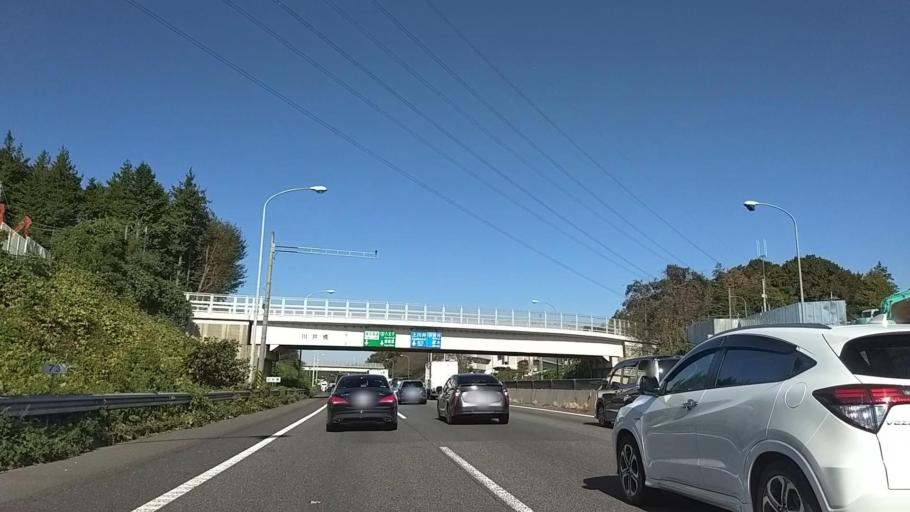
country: JP
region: Kanagawa
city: Minami-rinkan
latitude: 35.4895
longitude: 139.5059
